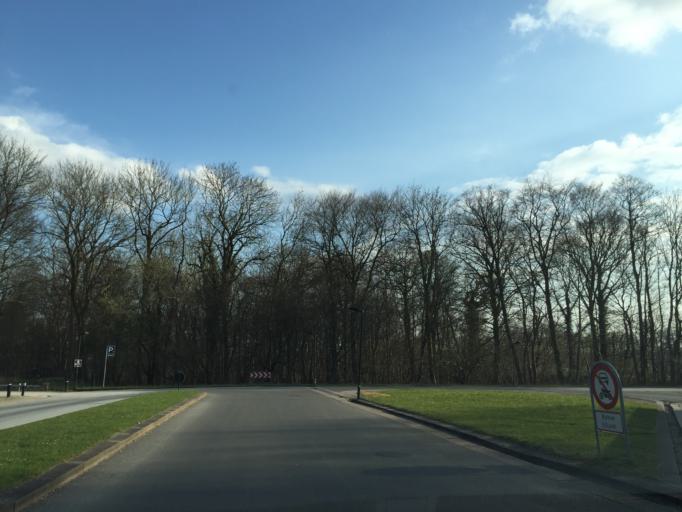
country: DK
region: South Denmark
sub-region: Odense Kommune
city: Neder Holluf
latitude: 55.3664
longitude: 10.4282
